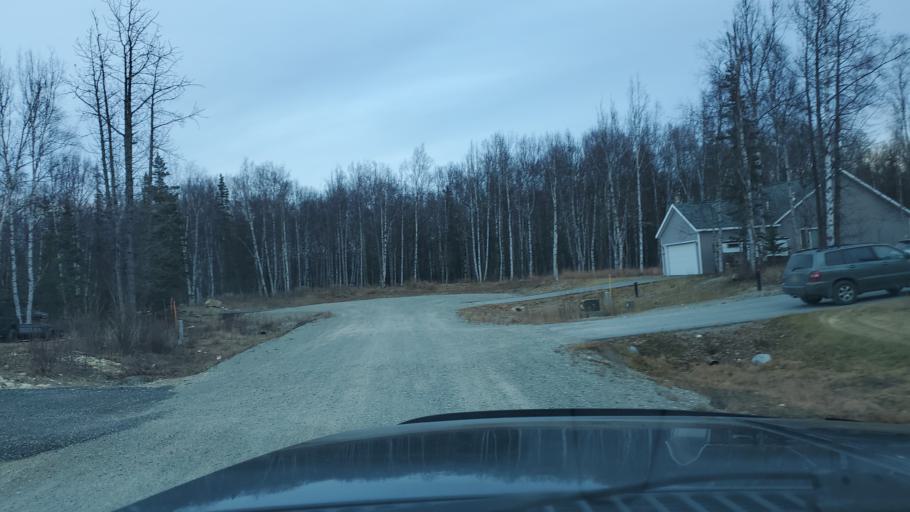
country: US
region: Alaska
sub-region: Matanuska-Susitna Borough
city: Lakes
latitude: 61.6542
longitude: -149.2906
